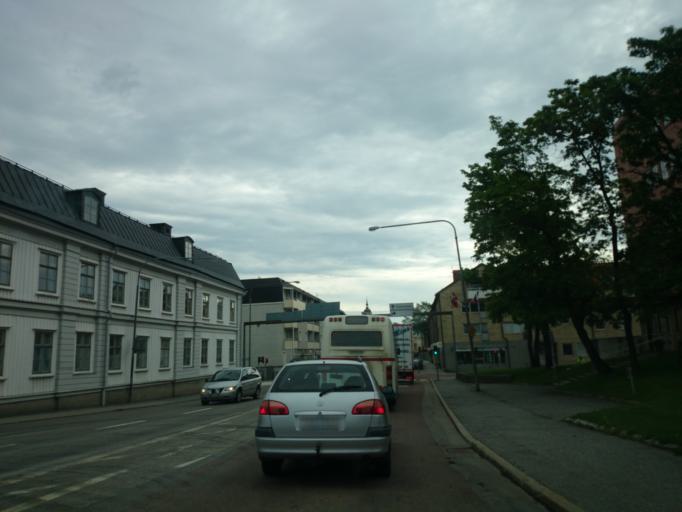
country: SE
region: Vaesternorrland
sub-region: Haernoesands Kommun
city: Haernoesand
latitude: 62.6293
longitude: 17.9324
